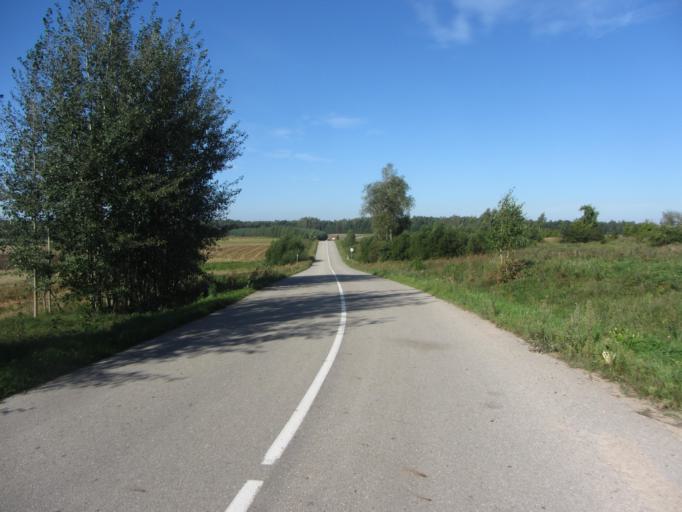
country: LT
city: Simnas
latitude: 54.3289
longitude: 23.7157
